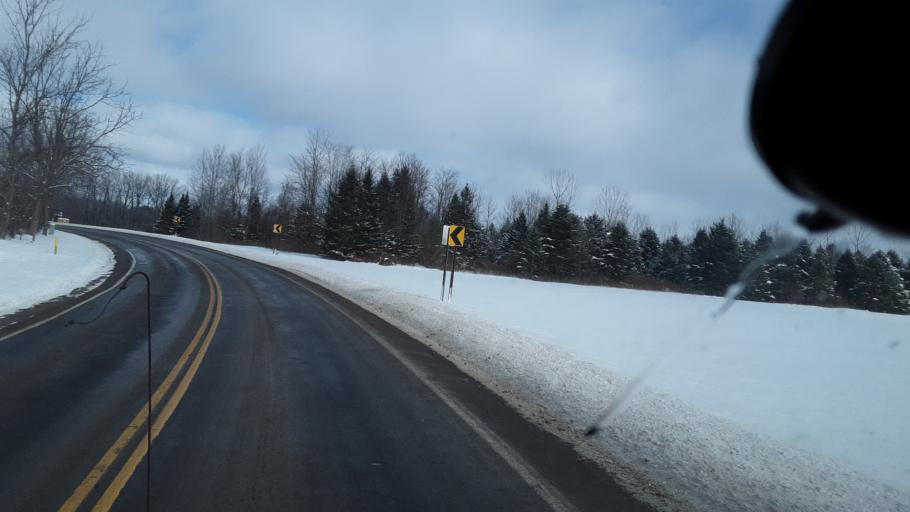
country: US
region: New York
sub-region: Wayne County
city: Newark
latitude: 43.0897
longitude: -77.0544
